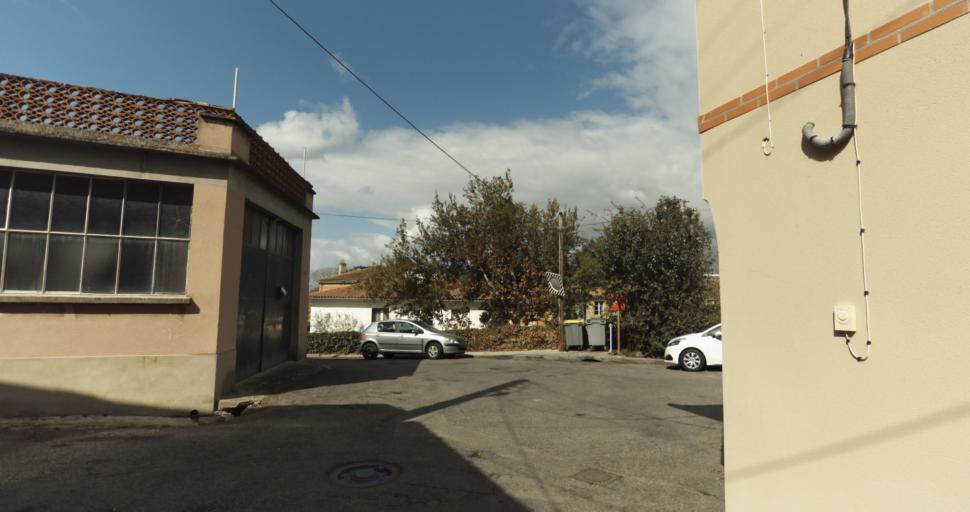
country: FR
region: Midi-Pyrenees
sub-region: Departement de la Haute-Garonne
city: Auterive
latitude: 43.3536
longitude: 1.4785
